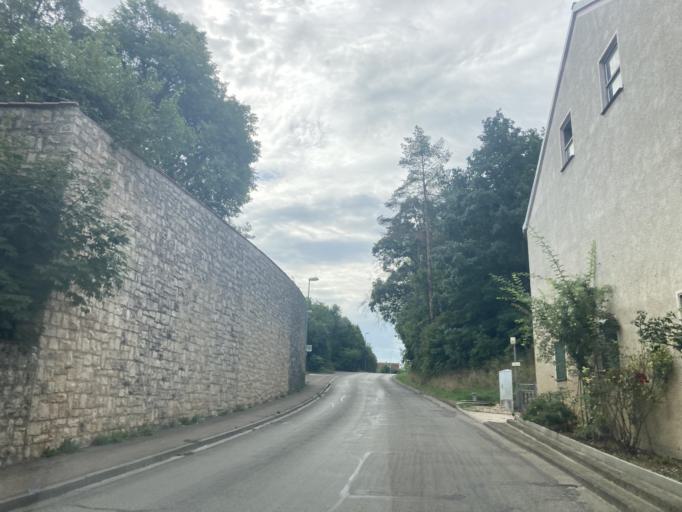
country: DE
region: Bavaria
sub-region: Swabia
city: Mottingen
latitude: 48.8124
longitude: 10.6035
